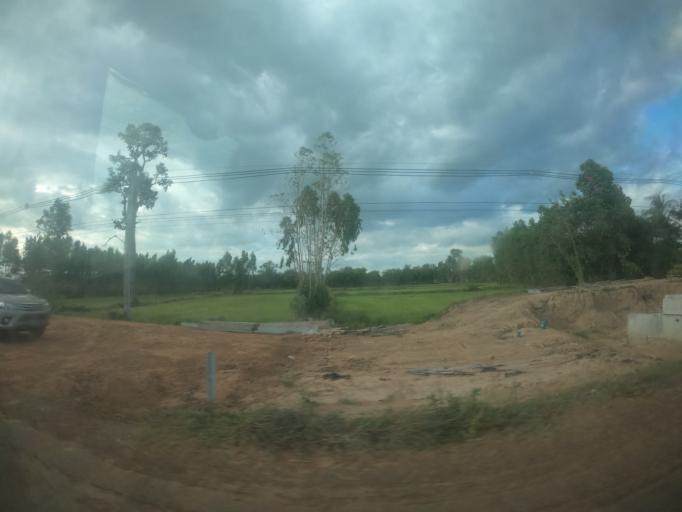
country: TH
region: Surin
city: Kap Choeng
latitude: 14.4575
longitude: 103.6725
